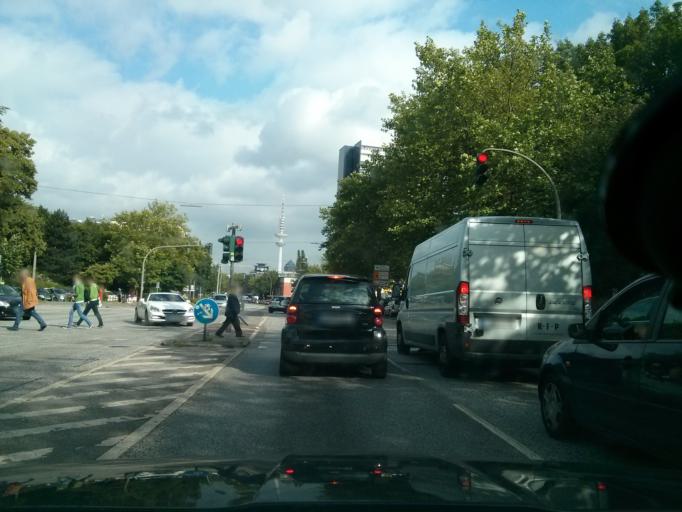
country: DE
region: Hamburg
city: St. Pauli
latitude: 53.5716
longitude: 9.9523
